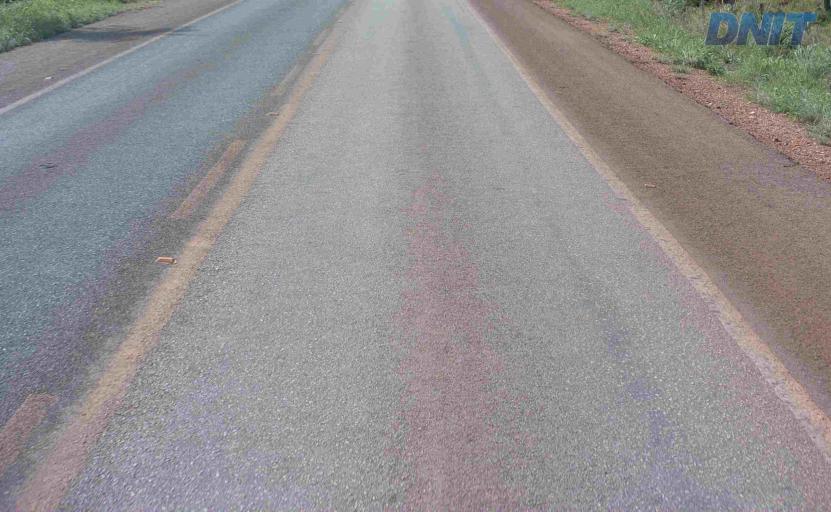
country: BR
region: Goias
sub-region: Barro Alto
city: Barro Alto
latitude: -15.0183
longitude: -48.8983
